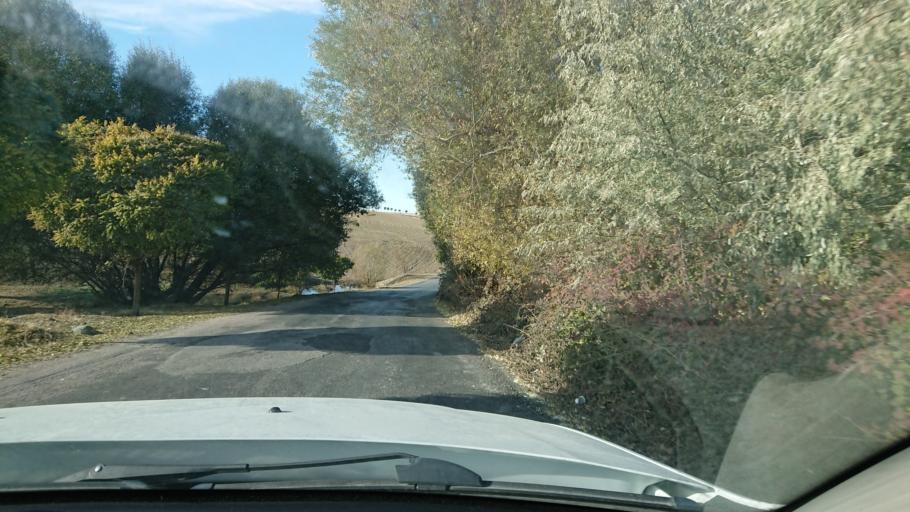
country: TR
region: Aksaray
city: Sariyahsi
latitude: 38.9699
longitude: 33.8671
